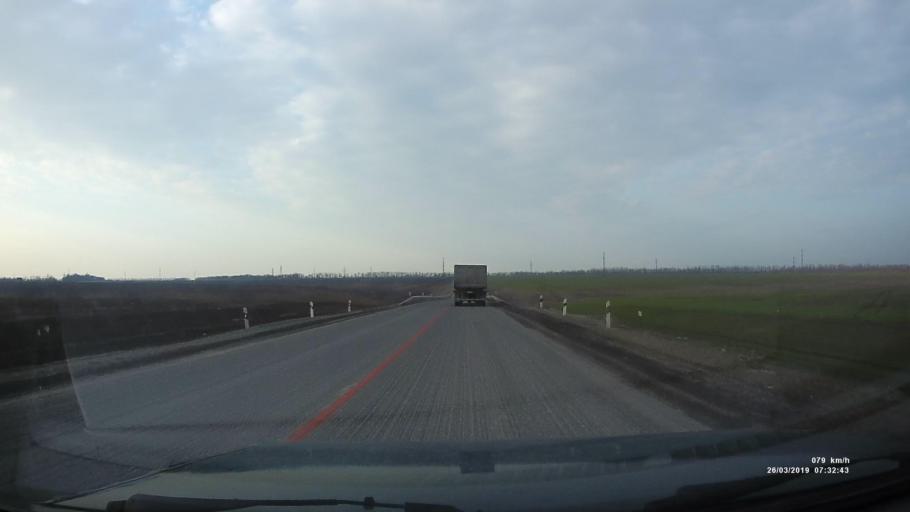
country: RU
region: Rostov
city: Novobessergenovka
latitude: 47.2226
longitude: 38.7755
